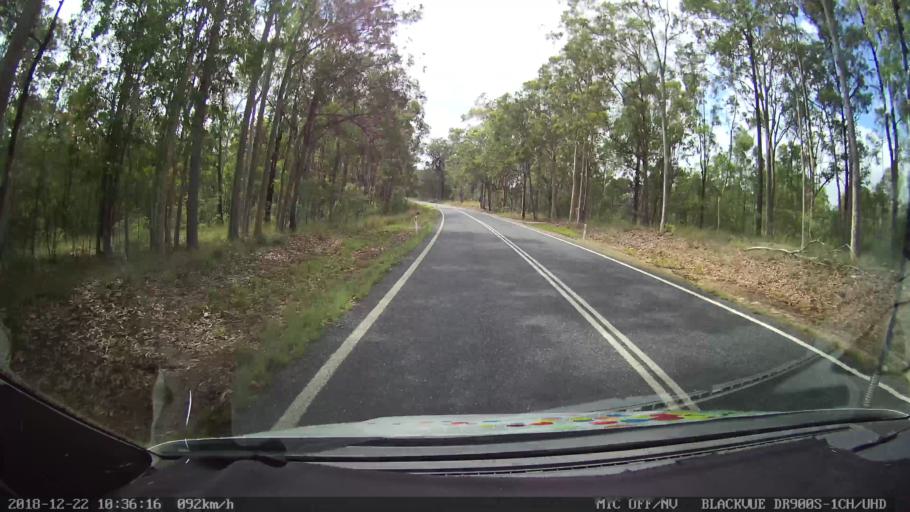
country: AU
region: New South Wales
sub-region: Clarence Valley
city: South Grafton
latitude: -29.6279
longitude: 152.6913
